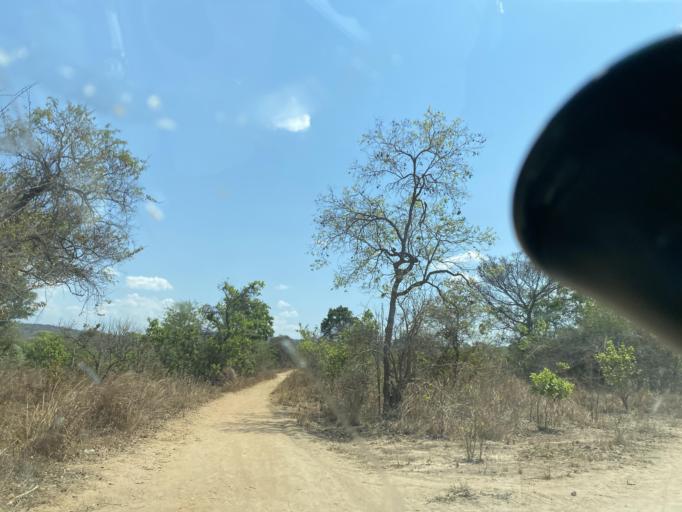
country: ZM
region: Lusaka
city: Chongwe
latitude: -15.0844
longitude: 29.4995
